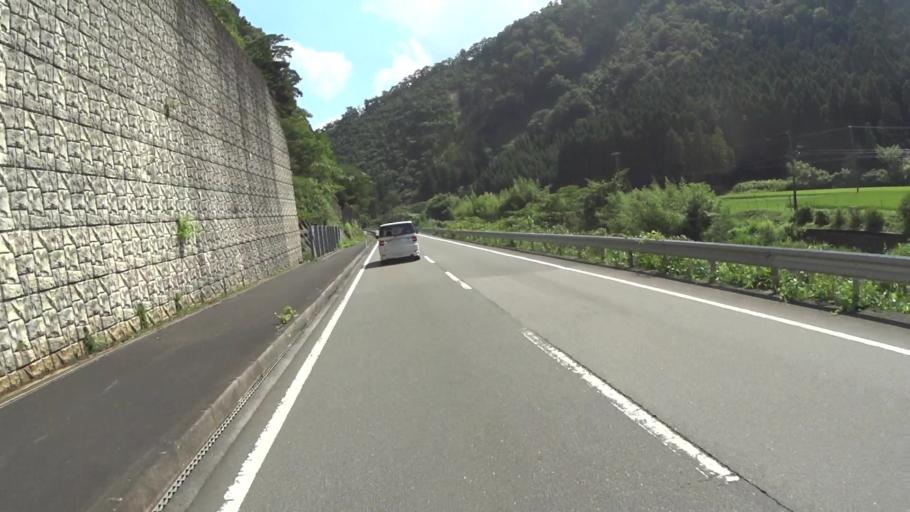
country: JP
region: Kyoto
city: Maizuru
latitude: 35.3077
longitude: 135.5556
